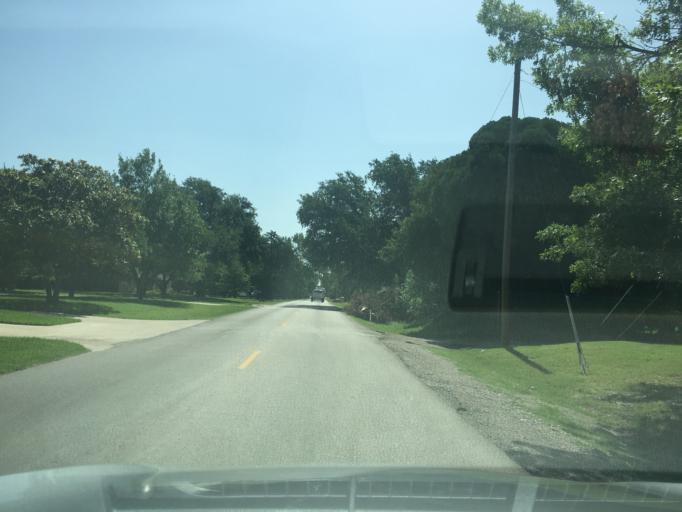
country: US
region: Texas
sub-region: Dallas County
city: University Park
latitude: 32.9022
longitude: -96.8097
